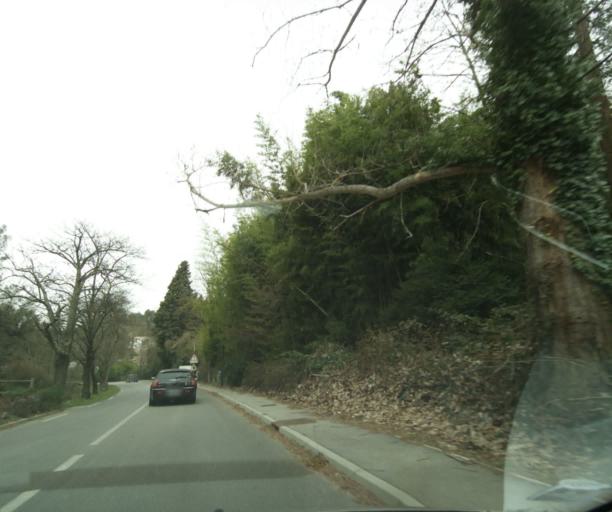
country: FR
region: Provence-Alpes-Cote d'Azur
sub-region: Departement des Bouches-du-Rhone
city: Saint-Marc-Jaumegarde
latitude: 43.5400
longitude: 5.4862
